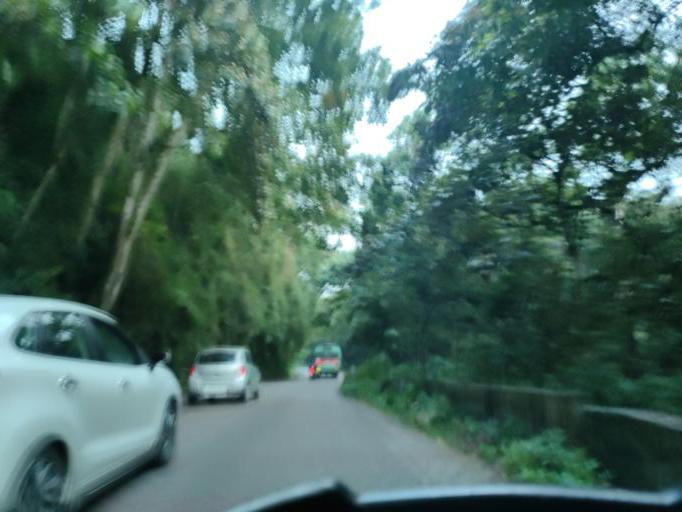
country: IN
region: Tamil Nadu
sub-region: Dindigul
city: Kodaikanal
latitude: 10.2496
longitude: 77.5207
